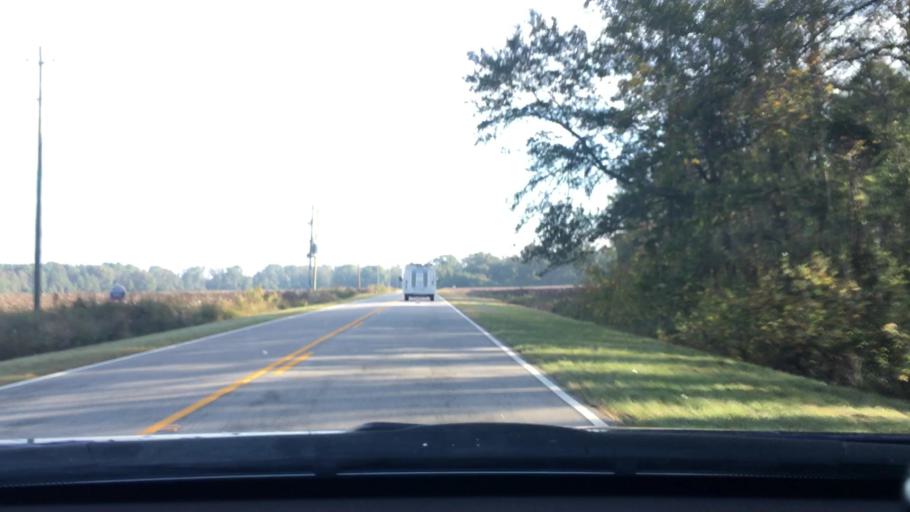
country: US
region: South Carolina
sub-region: Lee County
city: Bishopville
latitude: 34.0963
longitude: -80.1751
